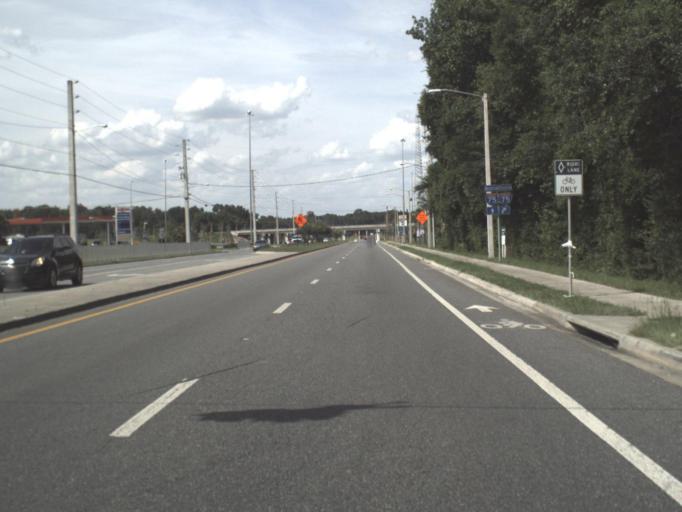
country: US
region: Florida
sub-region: Columbia County
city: Lake City
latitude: 30.1141
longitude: -82.6576
